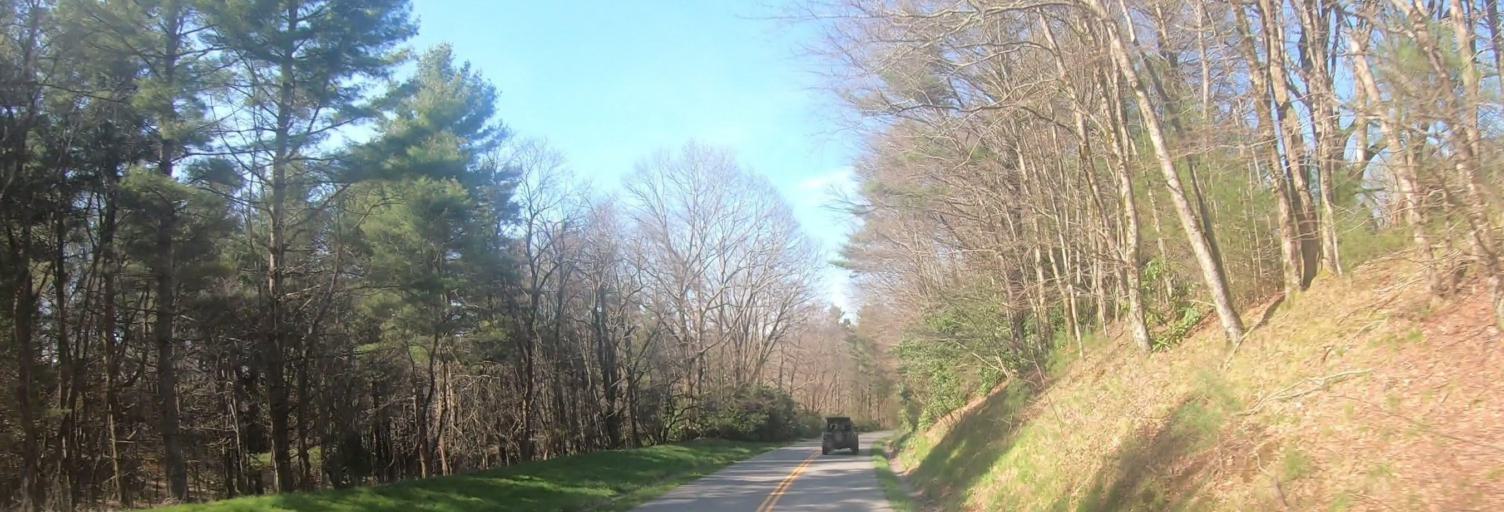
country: US
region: North Carolina
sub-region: Watauga County
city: Blowing Rock
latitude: 36.1547
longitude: -81.6221
